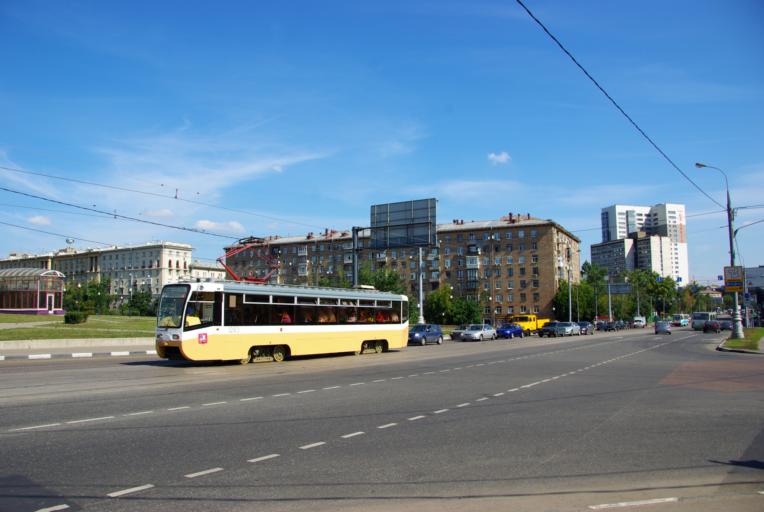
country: RU
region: Moscow
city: Novyye Cheremushki
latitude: 55.7062
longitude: 37.5876
